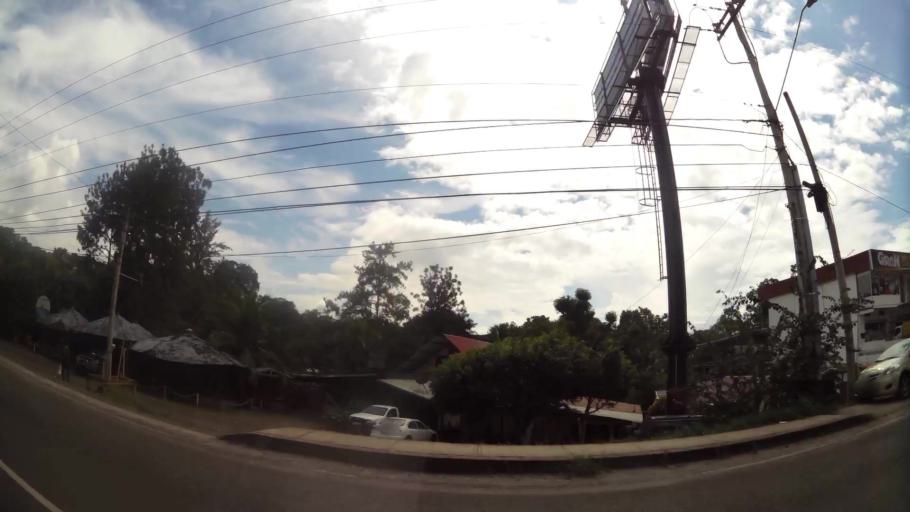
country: PA
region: Panama
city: Vista Alegre
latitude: 8.9359
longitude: -79.6857
